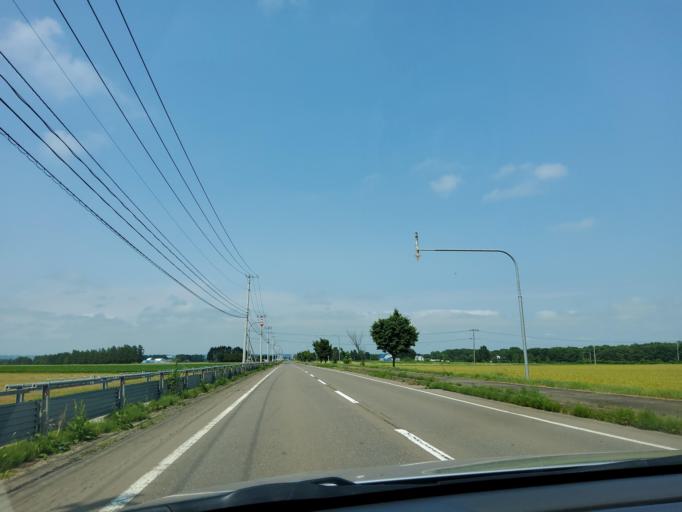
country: JP
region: Hokkaido
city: Obihiro
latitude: 42.8845
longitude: 143.0349
